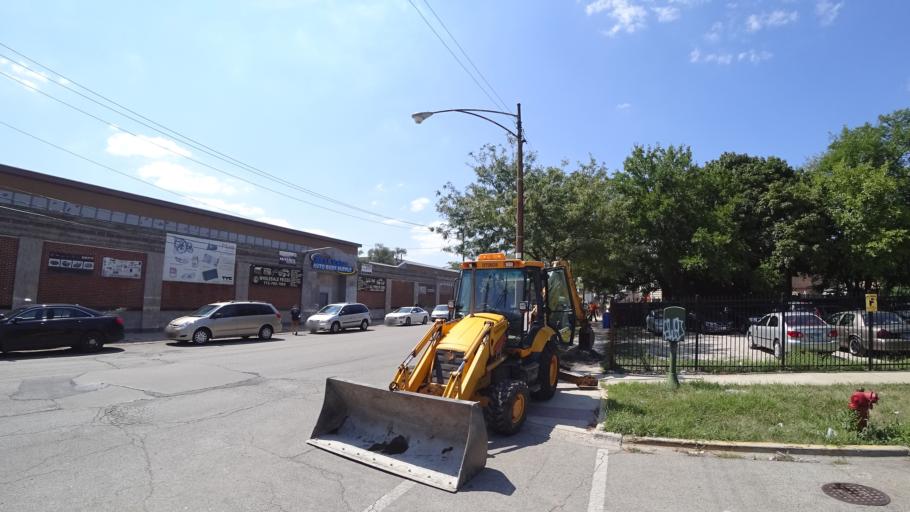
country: US
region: Illinois
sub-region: Cook County
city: Cicero
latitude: 41.8587
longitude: -87.7360
